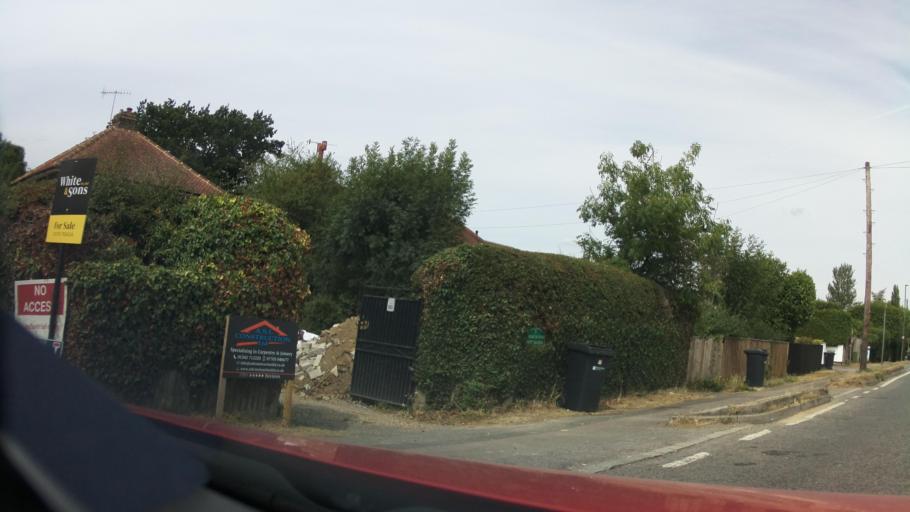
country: GB
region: England
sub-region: Surrey
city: Horley
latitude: 51.1695
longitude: -0.1896
